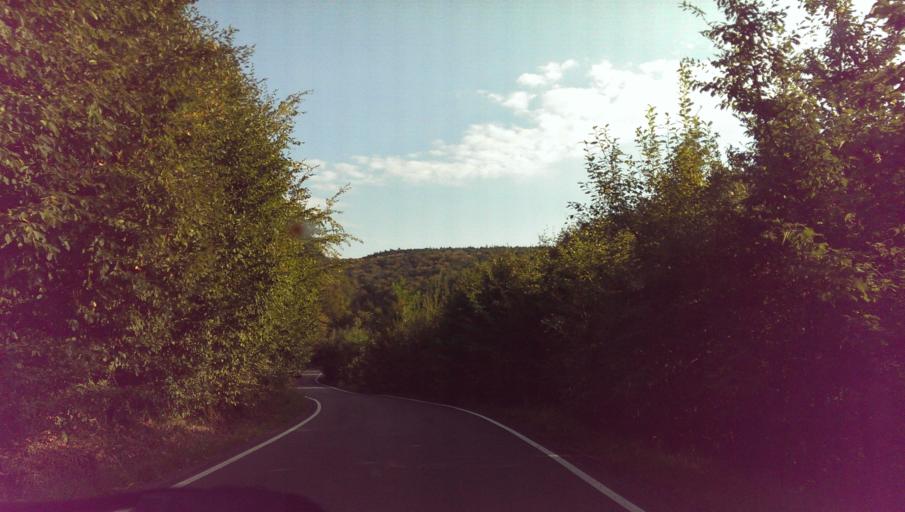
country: CZ
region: South Moravian
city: Zeravice
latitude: 49.0708
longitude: 17.2224
